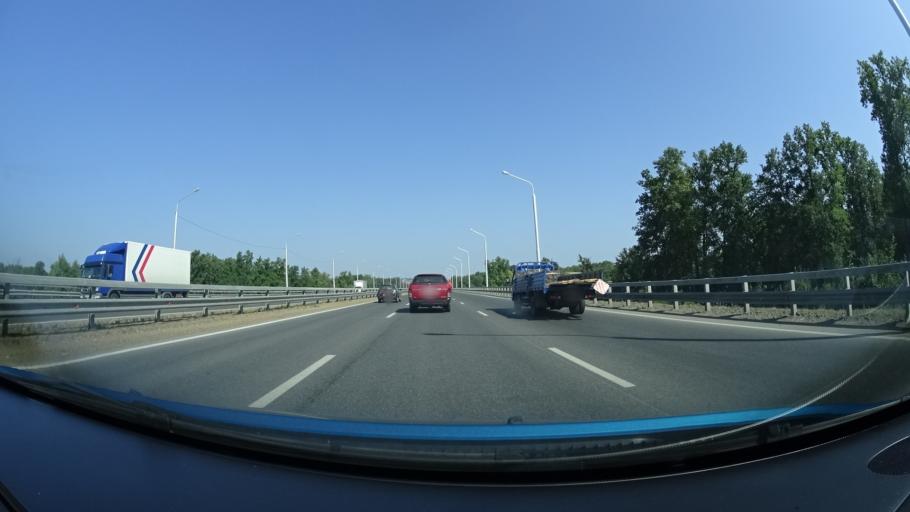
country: RU
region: Bashkortostan
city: Mikhaylovka
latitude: 54.7848
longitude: 55.9100
